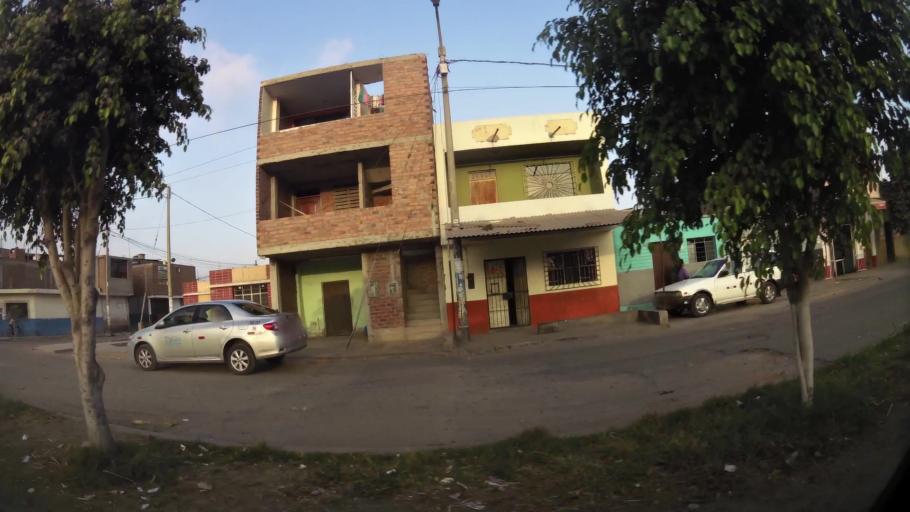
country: PE
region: La Libertad
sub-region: Provincia de Trujillo
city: El Porvenir
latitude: -8.0749
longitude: -78.9986
